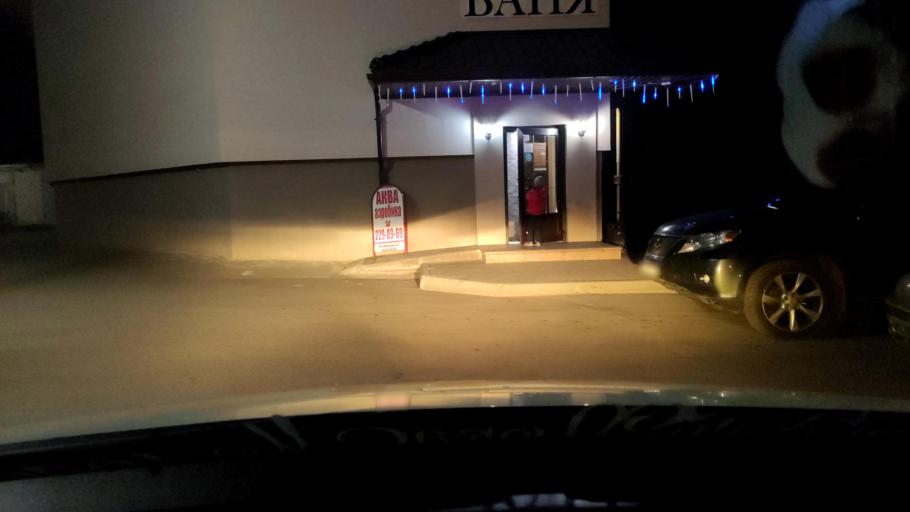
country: RU
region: Voronezj
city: Podgornoye
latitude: 51.7224
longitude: 39.1644
